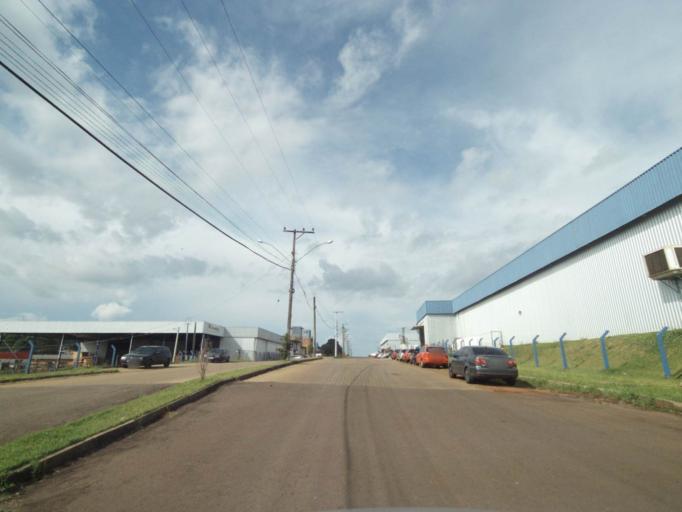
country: BR
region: Rio Grande do Sul
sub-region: Lagoa Vermelha
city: Lagoa Vermelha
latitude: -28.2241
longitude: -51.5102
